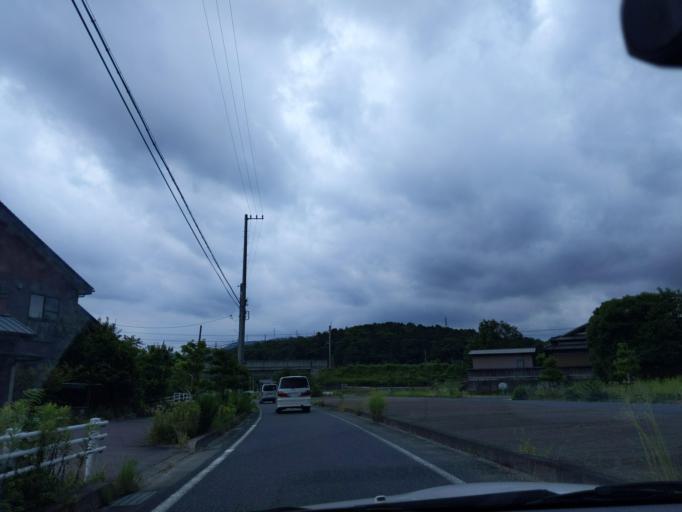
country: JP
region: Aichi
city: Seto
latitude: 35.1931
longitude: 137.1058
